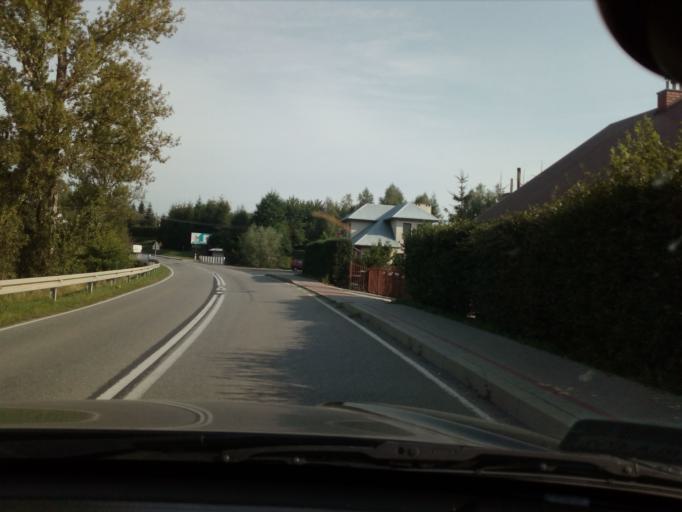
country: PL
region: Subcarpathian Voivodeship
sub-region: Powiat lancucki
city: Albigowa
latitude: 50.0396
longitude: 22.2304
